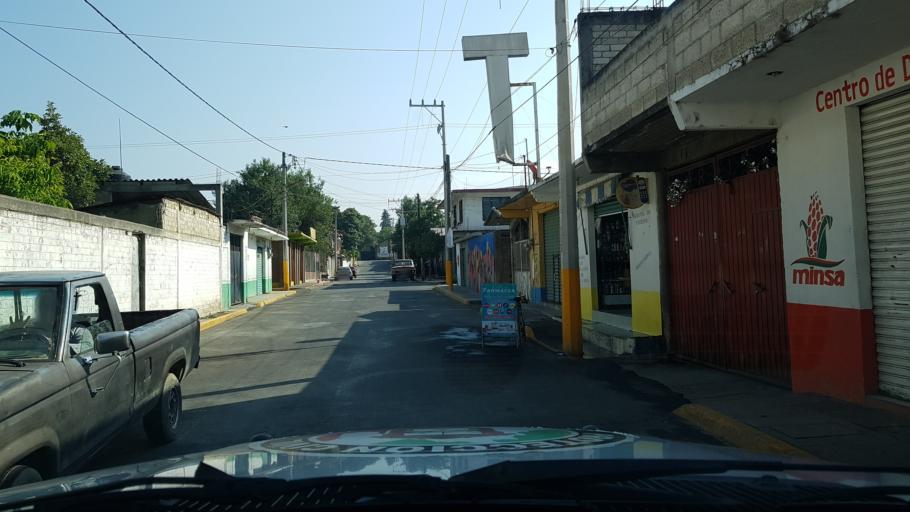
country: MX
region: Mexico
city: Atlautla
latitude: 19.0316
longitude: -98.7819
